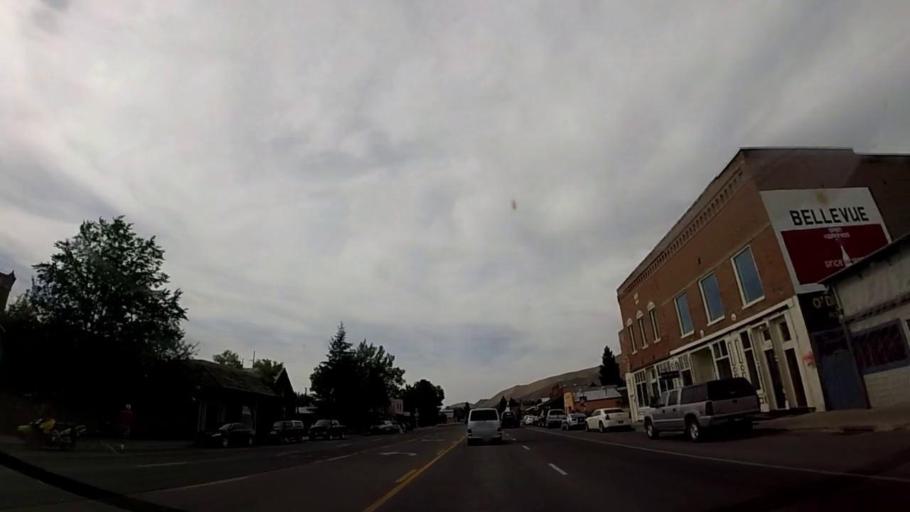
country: US
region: Idaho
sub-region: Blaine County
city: Bellevue
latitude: 43.4638
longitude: -114.2606
